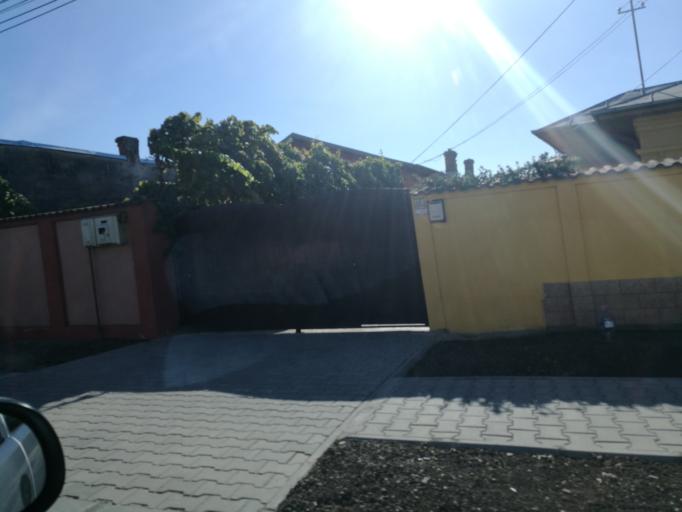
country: RO
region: Ilfov
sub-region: Comuna Dragomiresti-Vale
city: Dragomiresti-Deal
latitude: 44.4602
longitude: 25.9455
